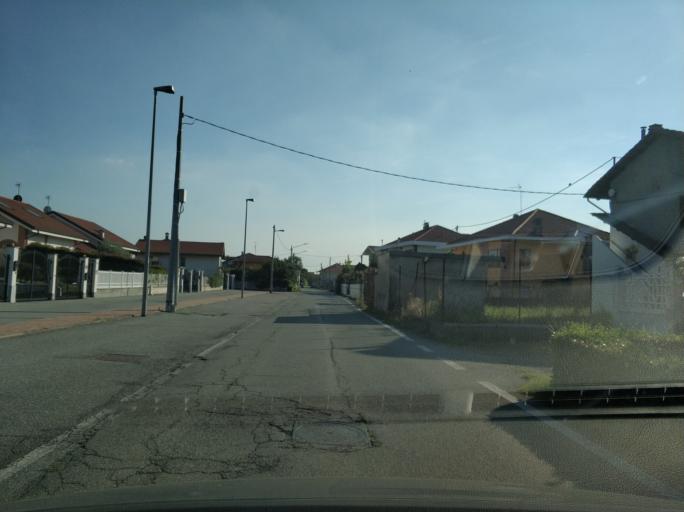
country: IT
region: Piedmont
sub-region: Provincia di Torino
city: San Maurizio
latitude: 45.2078
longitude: 7.6286
